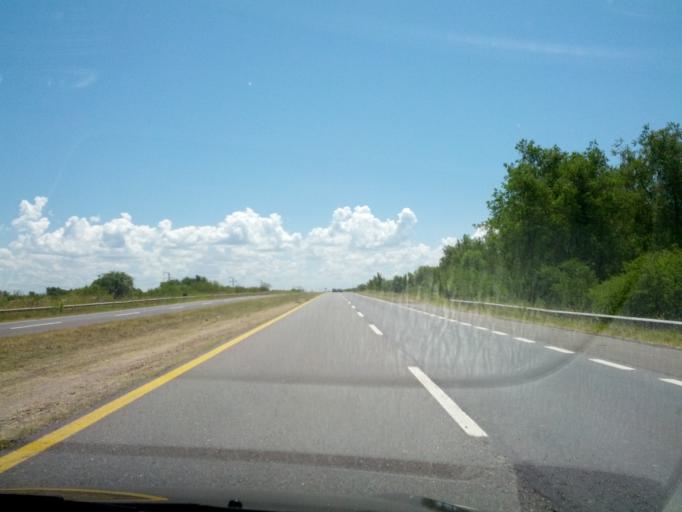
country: AR
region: Entre Rios
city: Villa Paranacito
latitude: -33.7367
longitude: -58.8546
